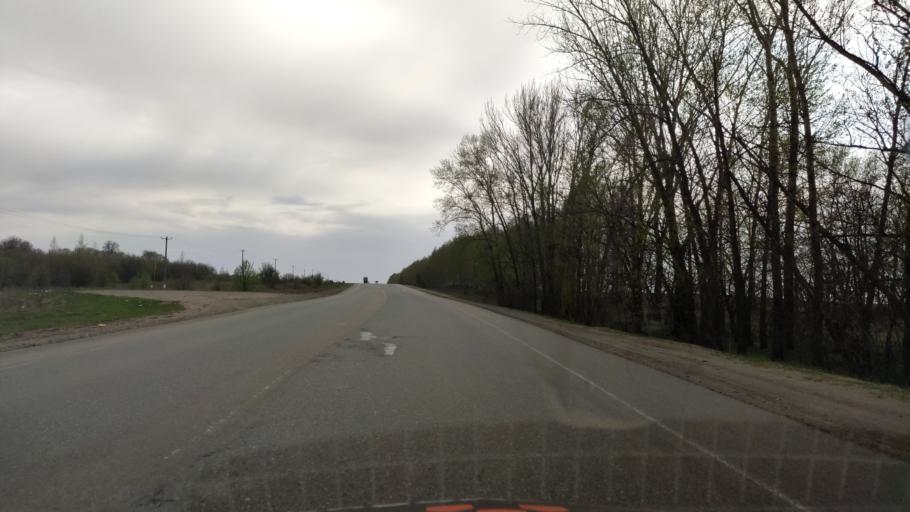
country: RU
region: Kursk
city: Gorshechnoye
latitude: 51.4625
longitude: 37.9256
